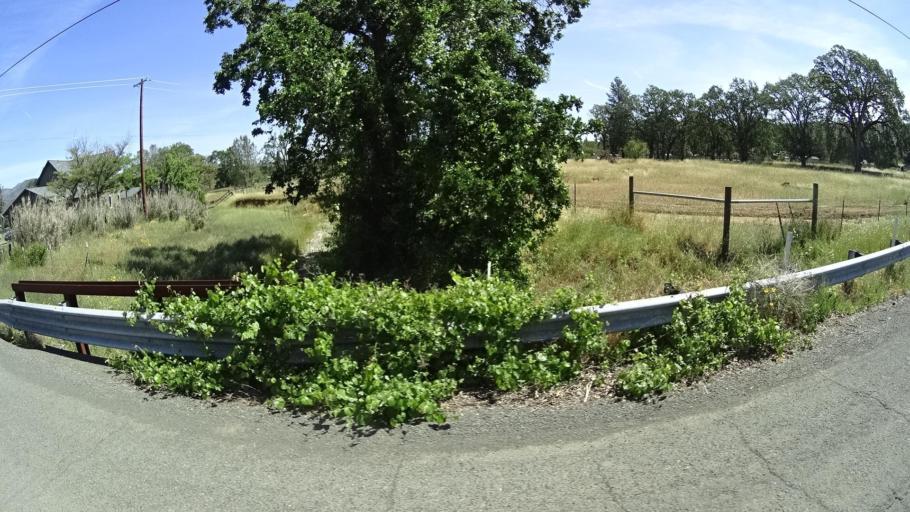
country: US
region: California
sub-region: Lake County
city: Middletown
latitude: 38.7400
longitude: -122.6294
